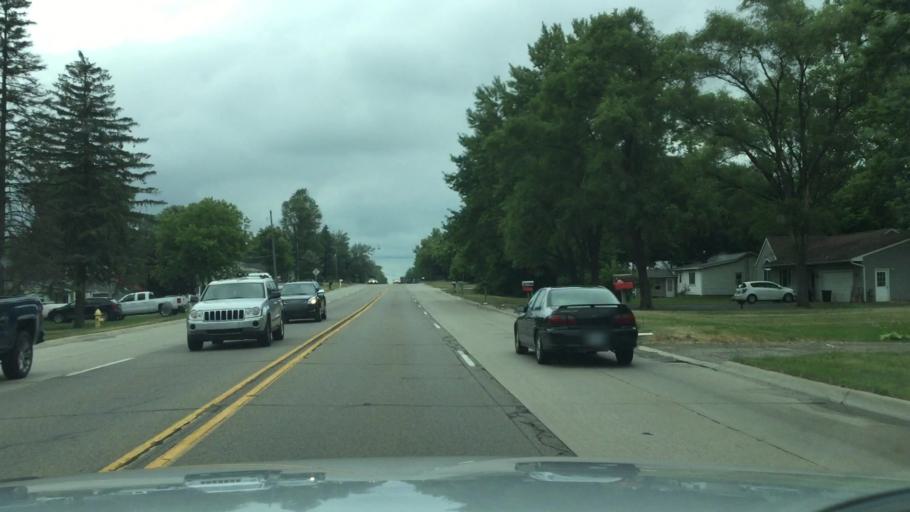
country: US
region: Michigan
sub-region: Genesee County
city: Burton
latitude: 43.0551
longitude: -83.6162
